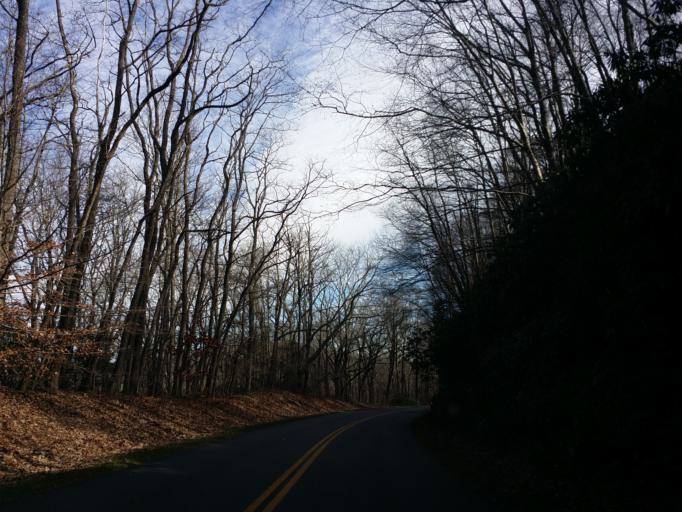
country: US
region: North Carolina
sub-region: Mitchell County
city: Spruce Pine
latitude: 35.8499
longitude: -82.0790
